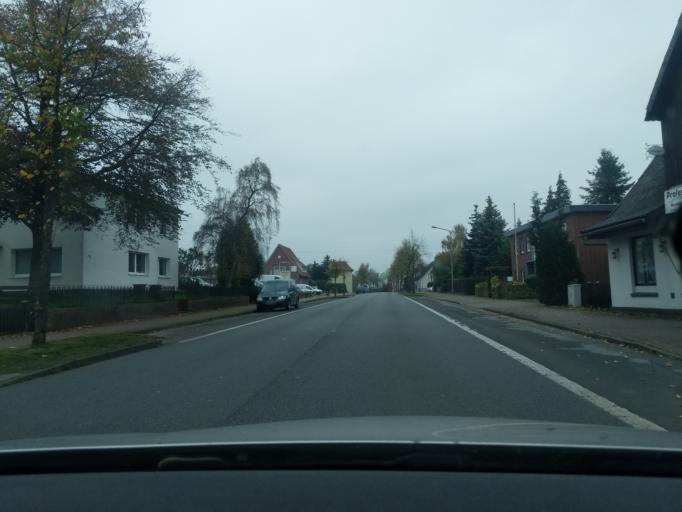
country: DE
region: Lower Saxony
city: Hemmoor
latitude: 53.6965
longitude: 9.1455
